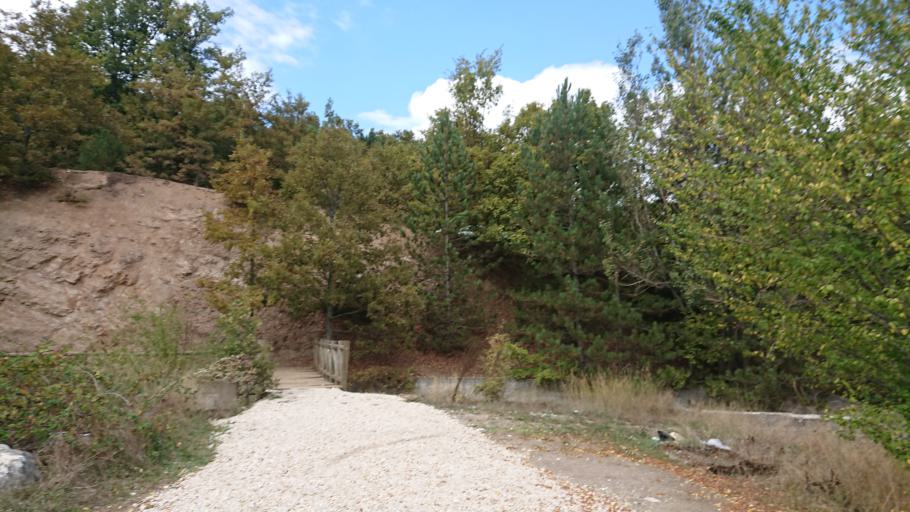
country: TR
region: Bilecik
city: Pazaryeri
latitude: 40.0173
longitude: 29.7970
